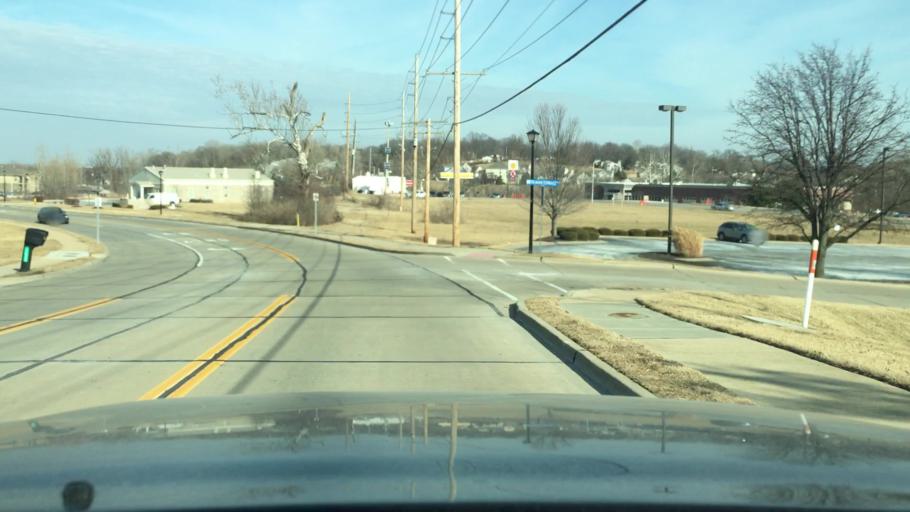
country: US
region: Missouri
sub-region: Saint Charles County
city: Saint Peters
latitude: 38.8037
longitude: -90.5564
